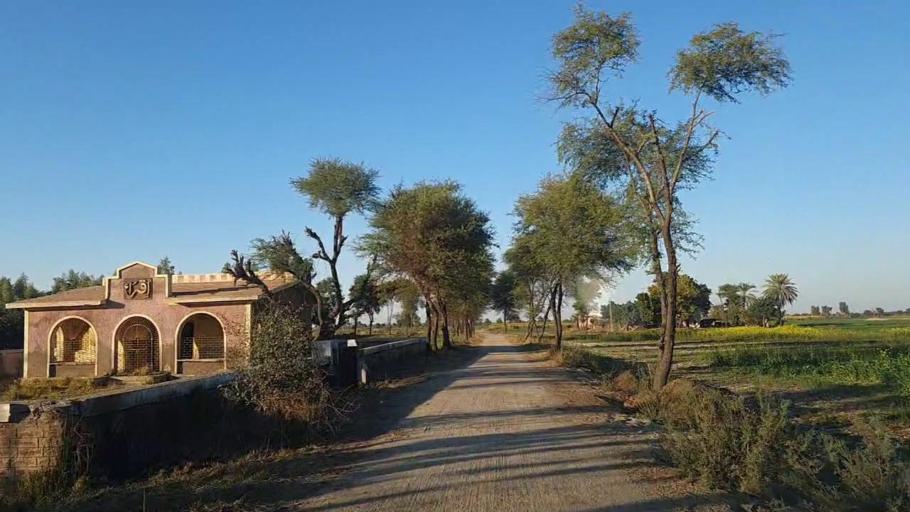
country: PK
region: Sindh
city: Sanghar
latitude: 26.1396
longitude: 68.9446
